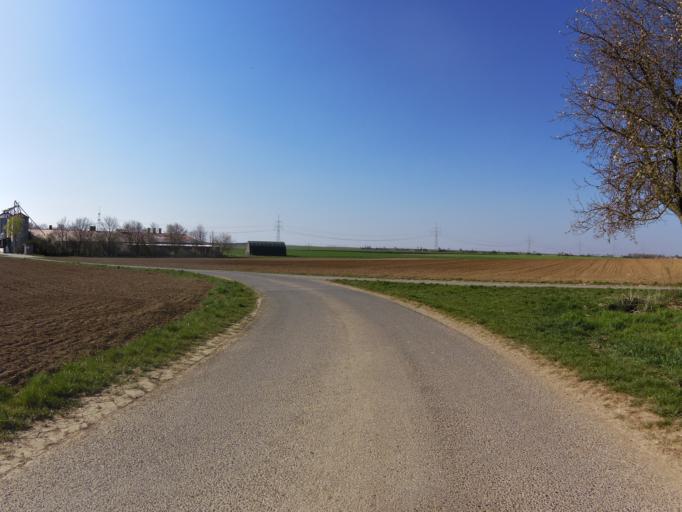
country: DE
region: Bavaria
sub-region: Regierungsbezirk Unterfranken
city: Prosselsheim
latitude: 49.8328
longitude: 10.1015
